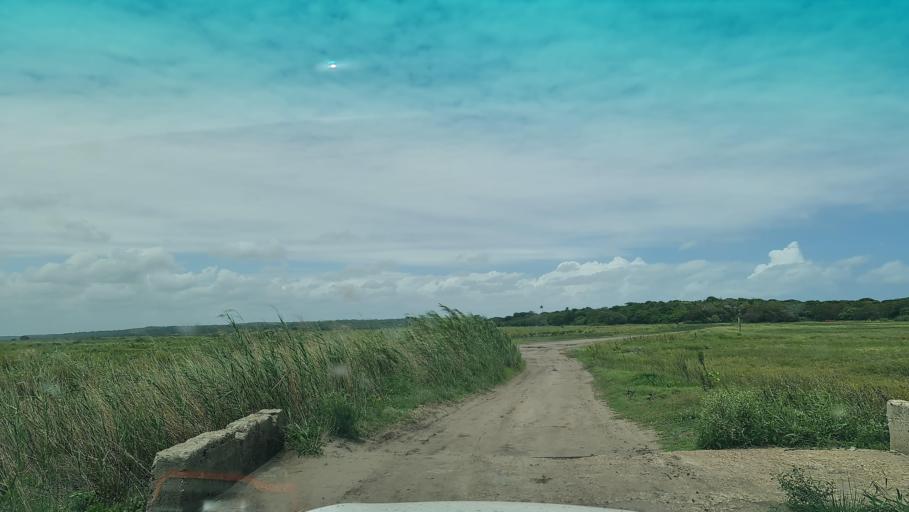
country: MZ
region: Maputo
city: Manhica
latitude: -25.5249
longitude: 32.8565
